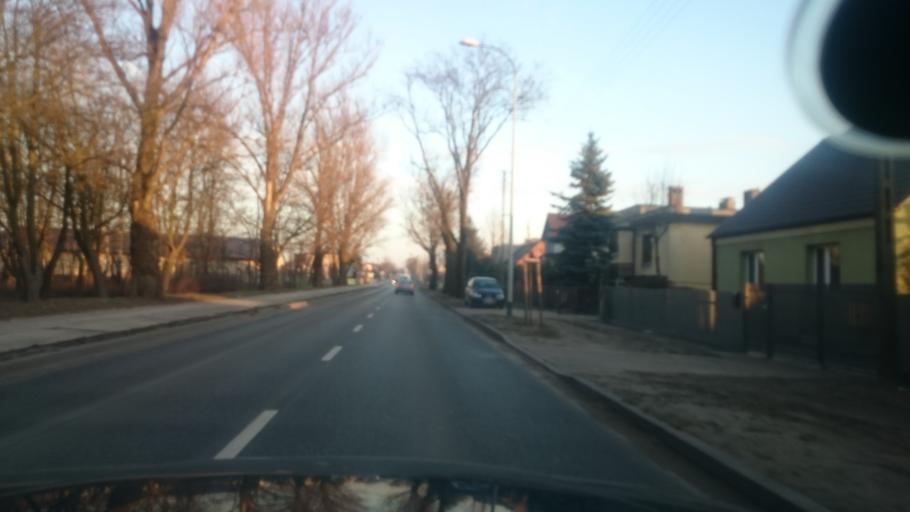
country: PL
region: Greater Poland Voivodeship
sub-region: Powiat ostrowski
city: Ostrow Wielkopolski
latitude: 51.6455
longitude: 17.8573
